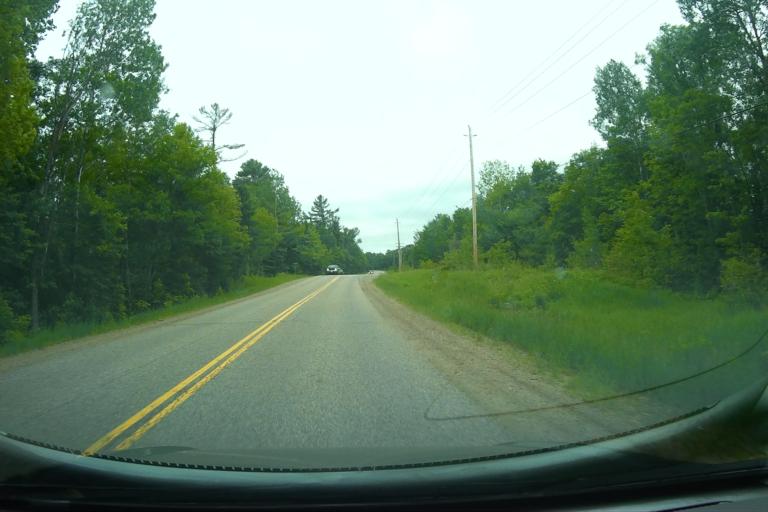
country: CA
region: Ontario
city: Pembroke
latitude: 45.4798
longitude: -77.2135
